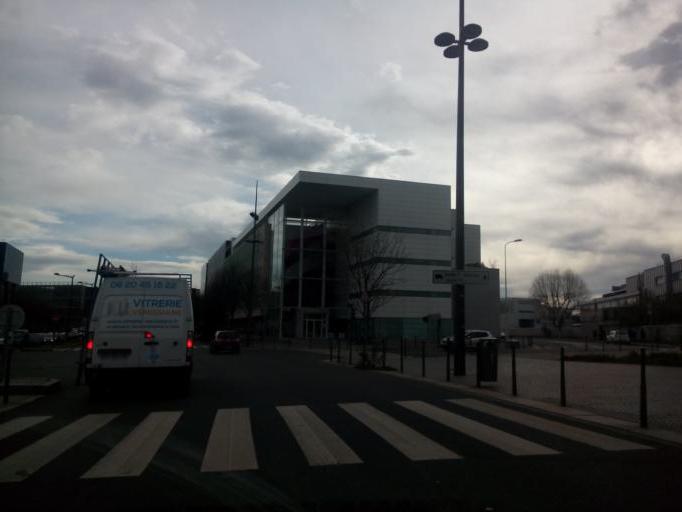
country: FR
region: Rhone-Alpes
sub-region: Departement du Rhone
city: La Mulatiere
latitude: 45.7284
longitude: 4.8238
